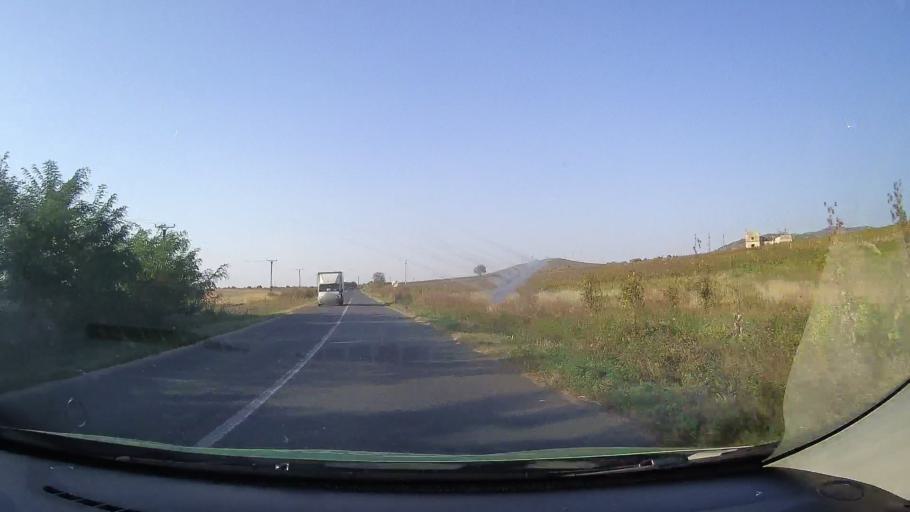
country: RO
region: Arad
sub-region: Comuna Siria
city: Siria
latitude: 46.2374
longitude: 21.6359
